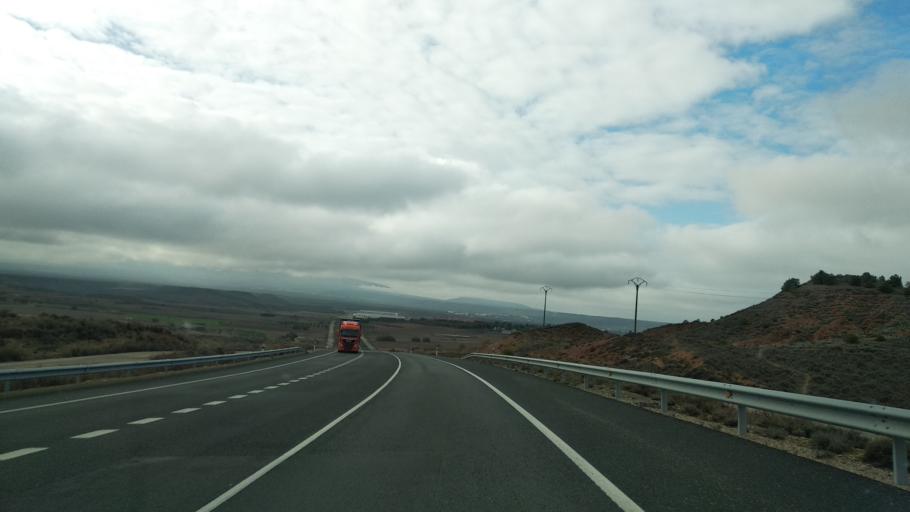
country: ES
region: La Rioja
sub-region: Provincia de La Rioja
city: Pradejon
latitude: 42.3210
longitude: -2.0196
